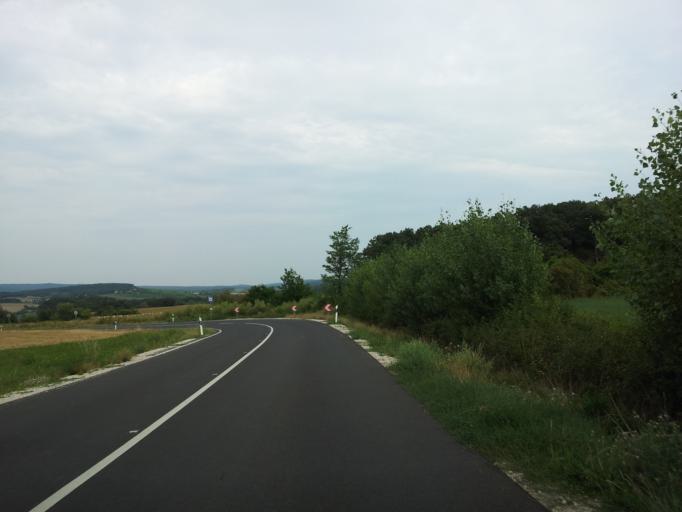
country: HU
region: Veszprem
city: Balatonfured
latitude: 46.9389
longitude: 17.7766
